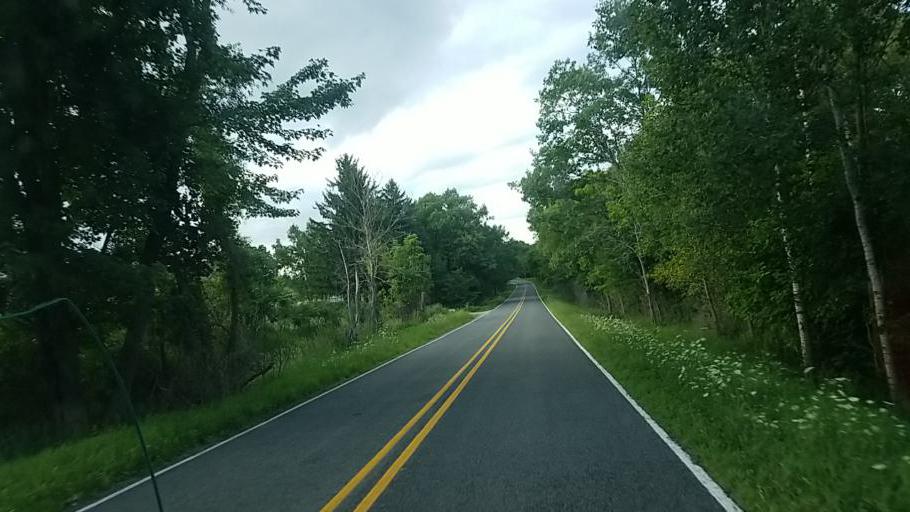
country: US
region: Michigan
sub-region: Montcalm County
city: Howard City
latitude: 43.3058
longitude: -85.3634
